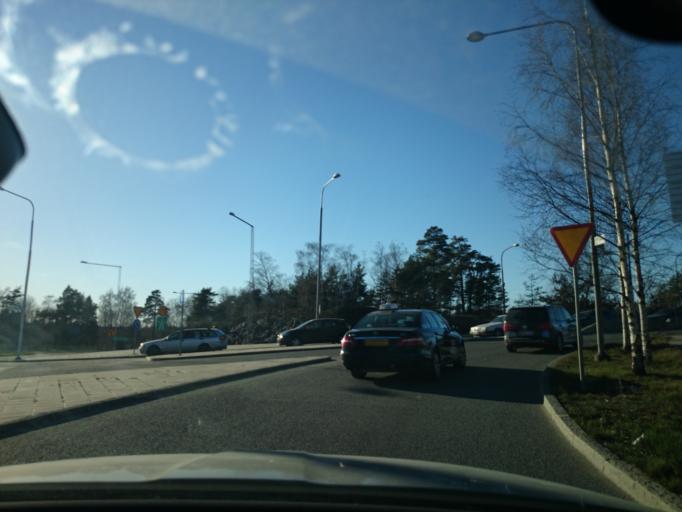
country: SE
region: Stockholm
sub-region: Huddinge Kommun
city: Huddinge
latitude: 59.2881
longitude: 17.9816
